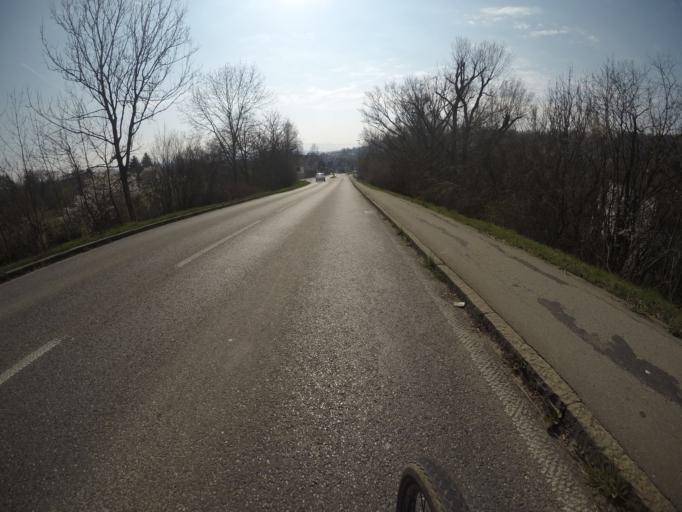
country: DE
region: Baden-Wuerttemberg
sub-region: Regierungsbezirk Stuttgart
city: Nurtingen
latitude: 48.6396
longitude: 9.3184
